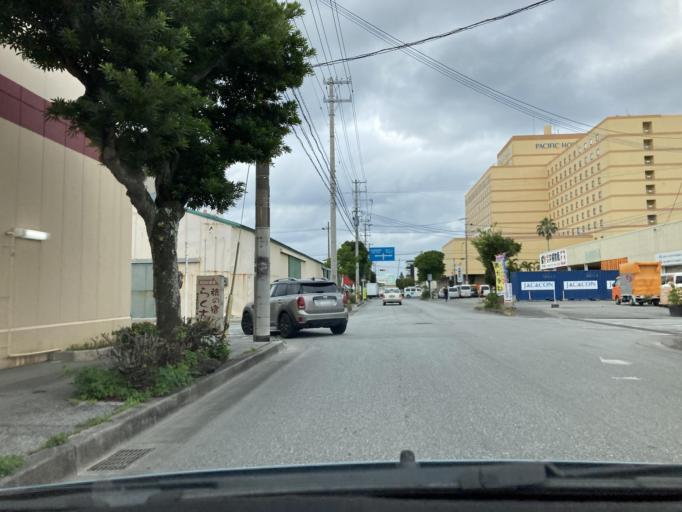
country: JP
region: Okinawa
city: Naha-shi
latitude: 26.2154
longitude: 127.6689
